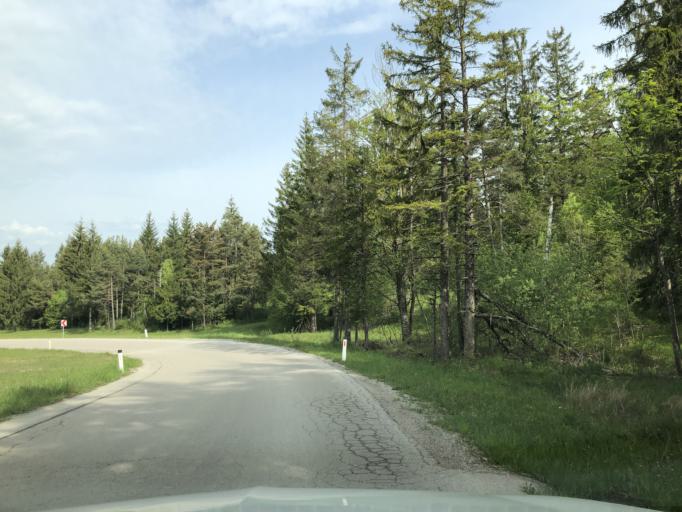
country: SI
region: Bloke
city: Nova Vas
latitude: 45.7984
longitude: 14.5385
